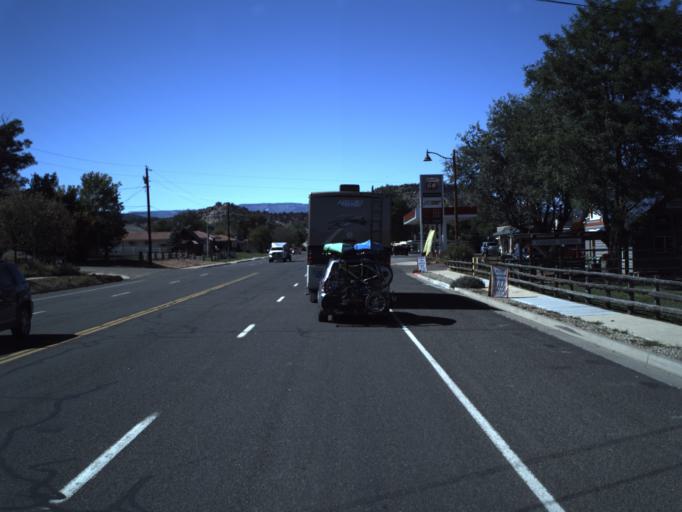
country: US
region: Utah
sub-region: Wayne County
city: Loa
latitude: 37.7703
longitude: -111.5974
